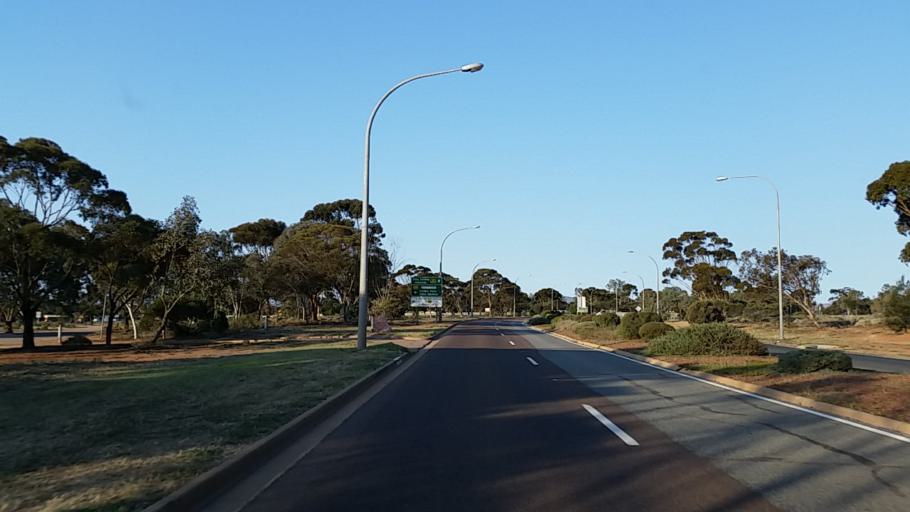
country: AU
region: South Australia
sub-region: Port Augusta
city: Port Augusta West
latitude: -32.4812
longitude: 137.7504
